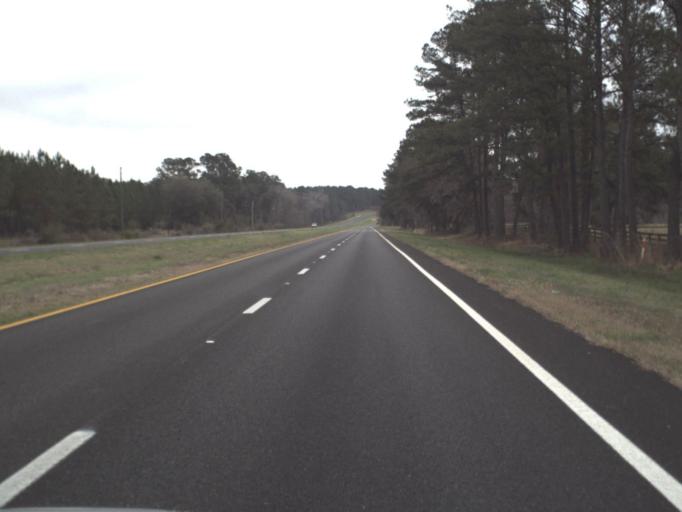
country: US
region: Florida
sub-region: Jefferson County
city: Monticello
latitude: 30.3875
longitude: -83.8448
